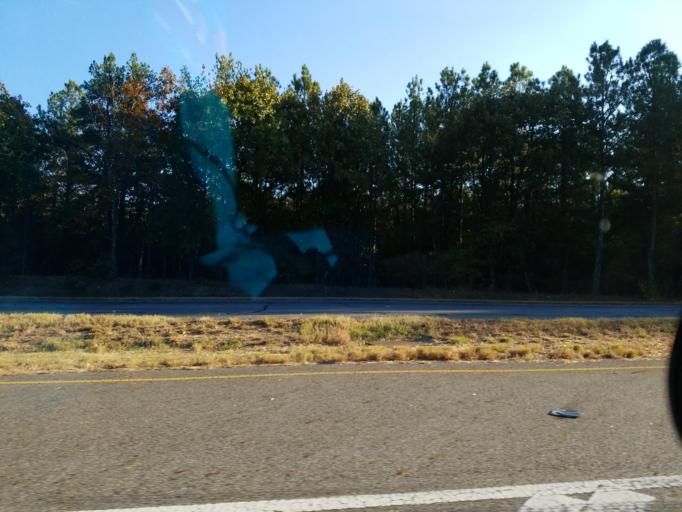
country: US
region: Georgia
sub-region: Bartow County
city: Euharlee
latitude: 34.2223
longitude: -84.9079
